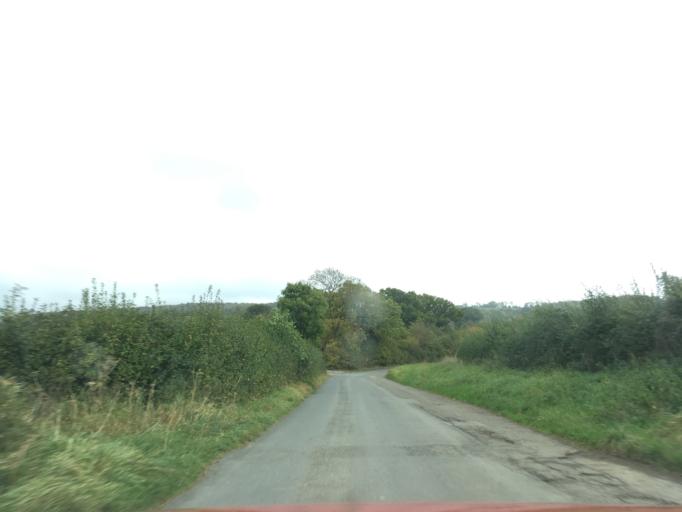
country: GB
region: England
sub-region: Gloucestershire
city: Stonehouse
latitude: 51.7561
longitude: -2.2750
